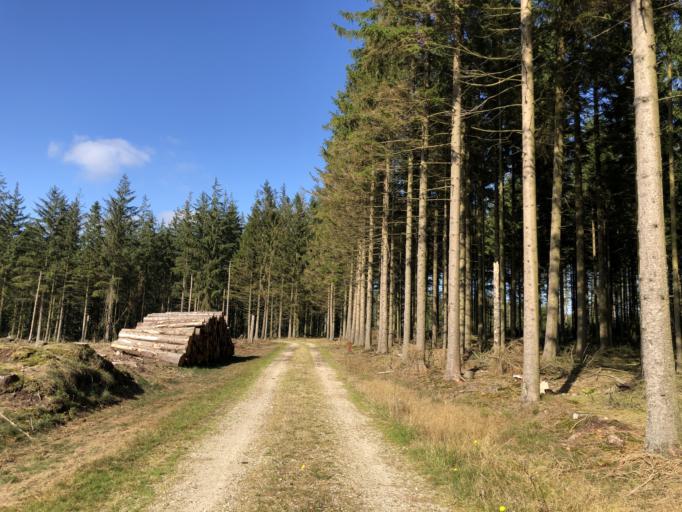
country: DK
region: Central Jutland
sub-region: Holstebro Kommune
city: Holstebro
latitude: 56.2483
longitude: 8.5008
